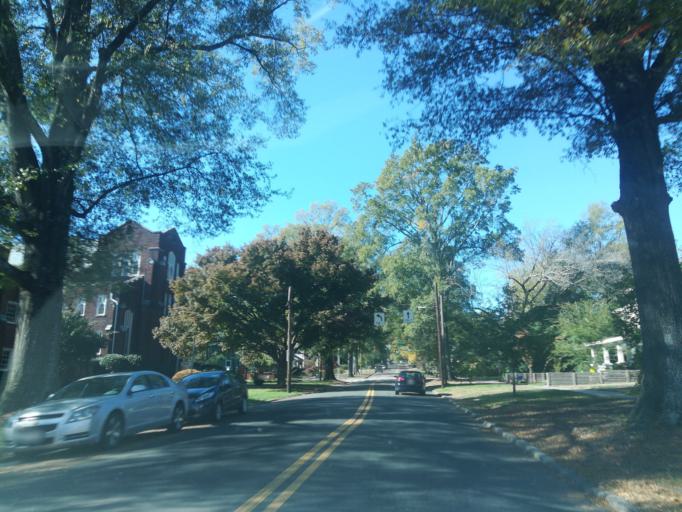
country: US
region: North Carolina
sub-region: Durham County
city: Durham
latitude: 36.0056
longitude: -78.9072
